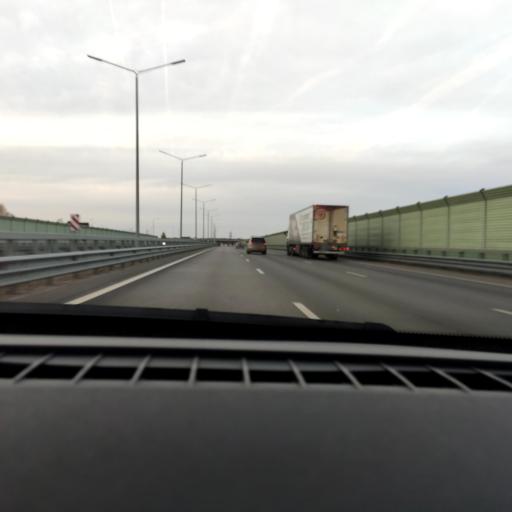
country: RU
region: Voronezj
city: Ramon'
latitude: 51.8190
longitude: 39.2522
